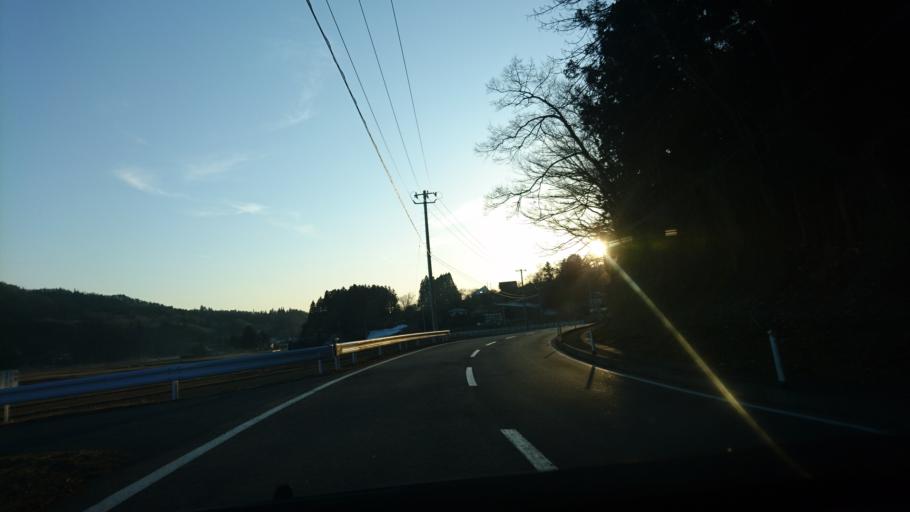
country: JP
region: Iwate
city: Mizusawa
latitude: 39.0461
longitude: 141.3595
